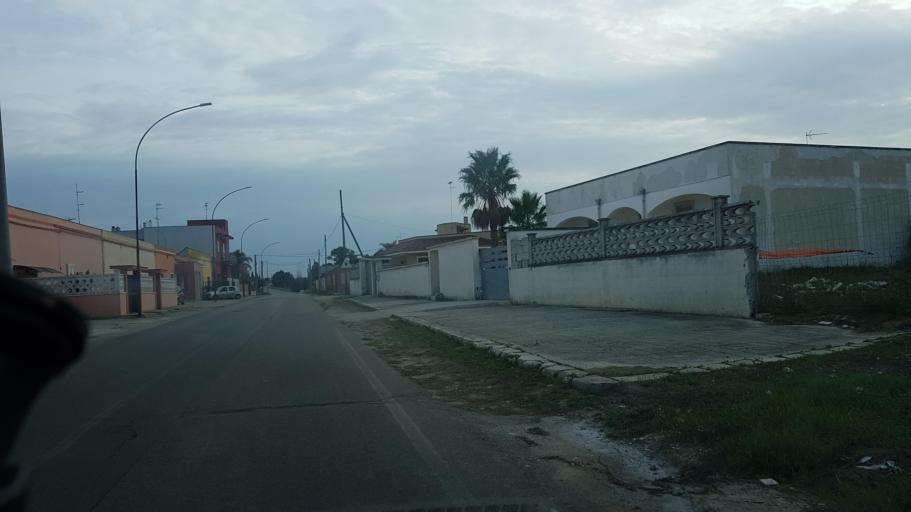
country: IT
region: Apulia
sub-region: Provincia di Lecce
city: Trepuzzi
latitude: 40.4164
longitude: 18.0735
